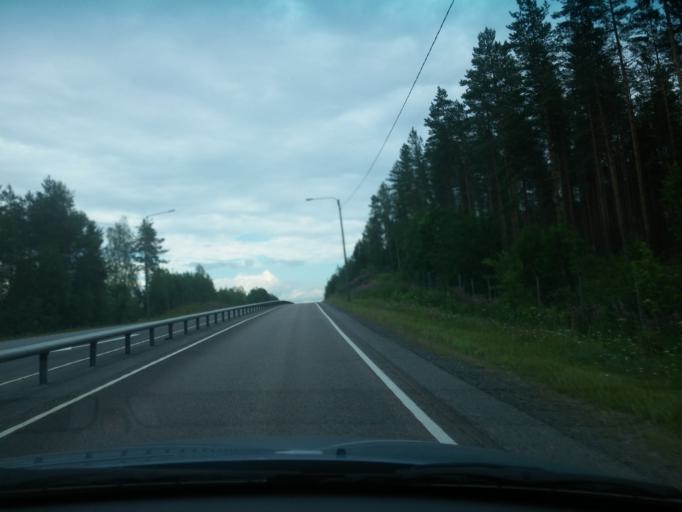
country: FI
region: Haeme
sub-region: Riihimaeki
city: Loppi
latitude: 60.7327
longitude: 24.5375
